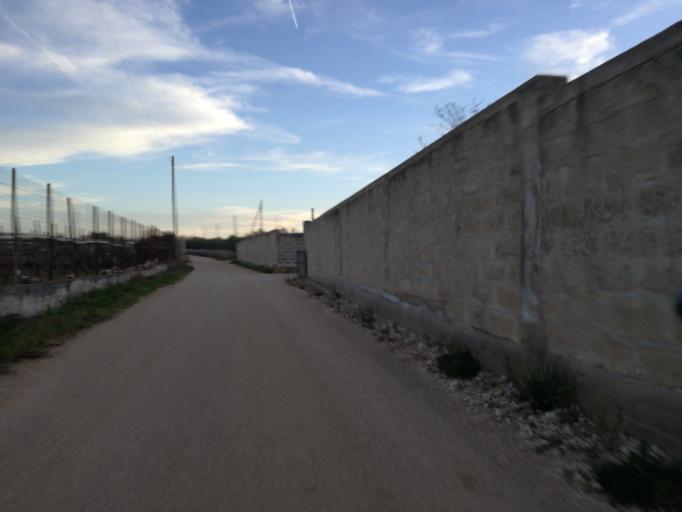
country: IT
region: Apulia
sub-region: Provincia di Bari
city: Adelfia
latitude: 41.0184
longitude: 16.8719
